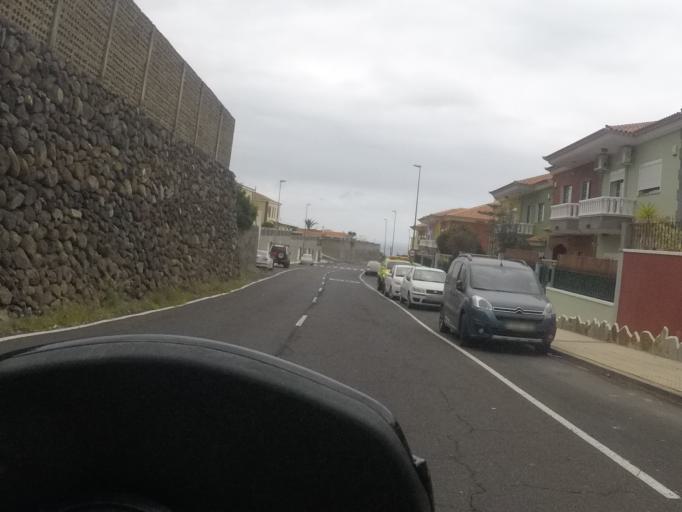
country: ES
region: Canary Islands
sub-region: Provincia de Santa Cruz de Tenerife
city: Candelaria
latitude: 28.3497
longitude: -16.3781
